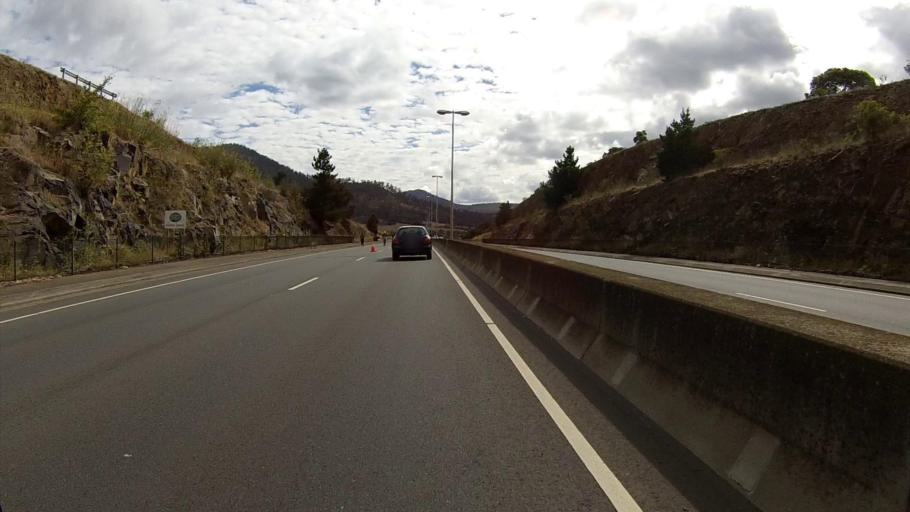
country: AU
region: Tasmania
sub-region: Glenorchy
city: Goodwood
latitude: -42.8221
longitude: 147.3019
